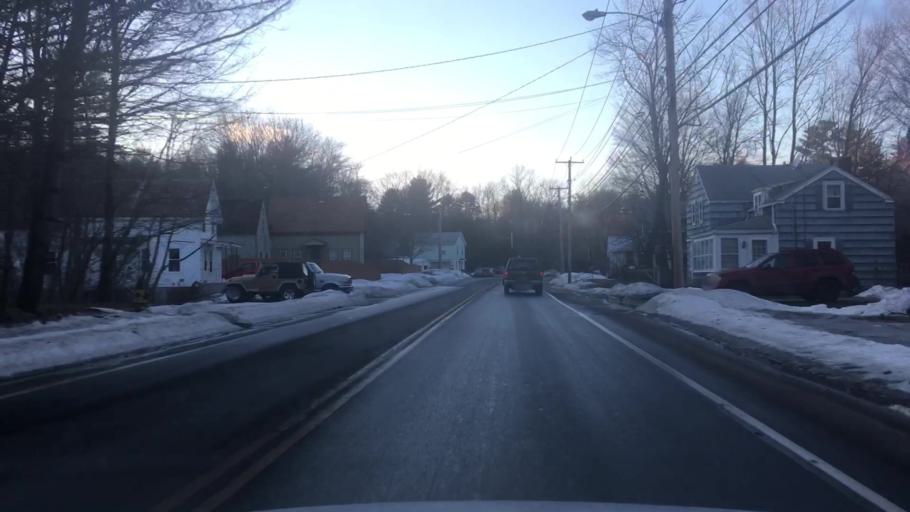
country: US
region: Maine
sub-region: York County
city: Springvale
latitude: 43.4717
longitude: -70.8082
